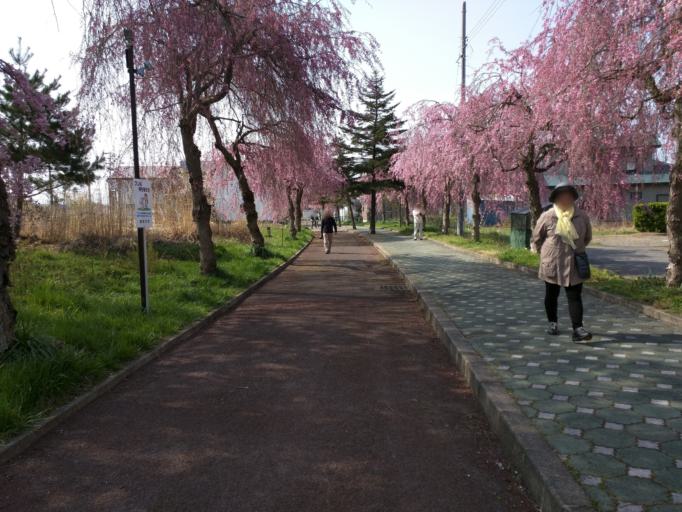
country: JP
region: Fukushima
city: Kitakata
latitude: 37.6474
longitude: 139.8623
